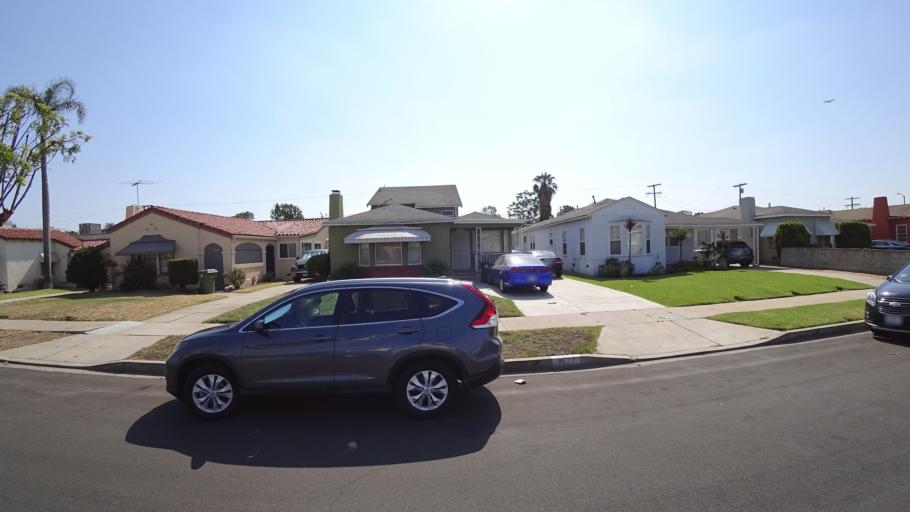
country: US
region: California
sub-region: Los Angeles County
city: Westmont
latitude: 33.9553
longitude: -118.3145
